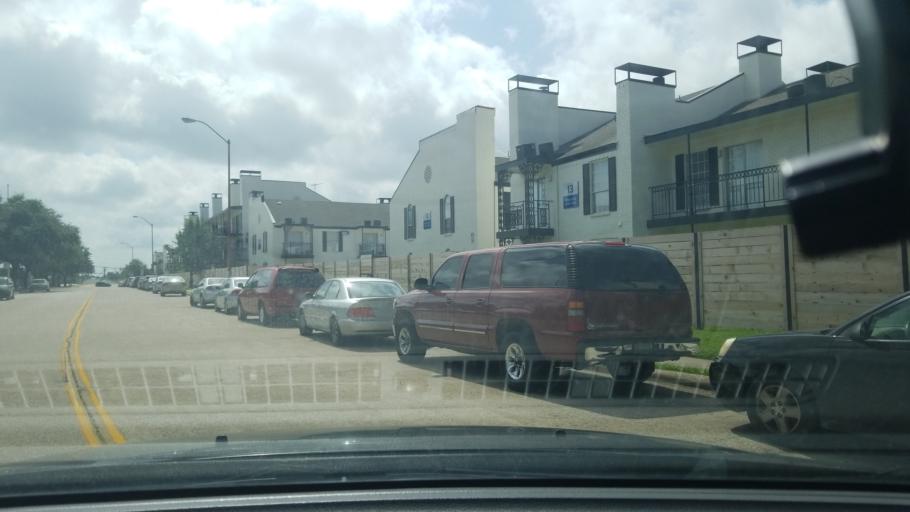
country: US
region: Texas
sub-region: Dallas County
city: Mesquite
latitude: 32.8028
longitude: -96.6908
